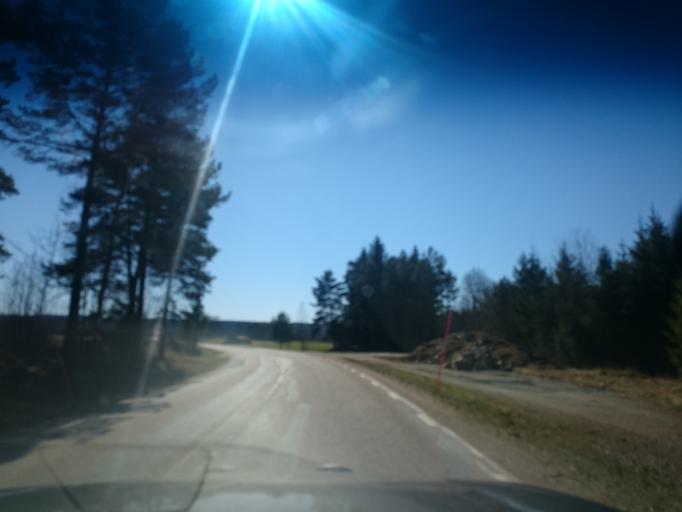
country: SE
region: Joenkoeping
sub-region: Vetlanda Kommun
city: Landsbro
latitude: 57.2131
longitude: 14.9454
